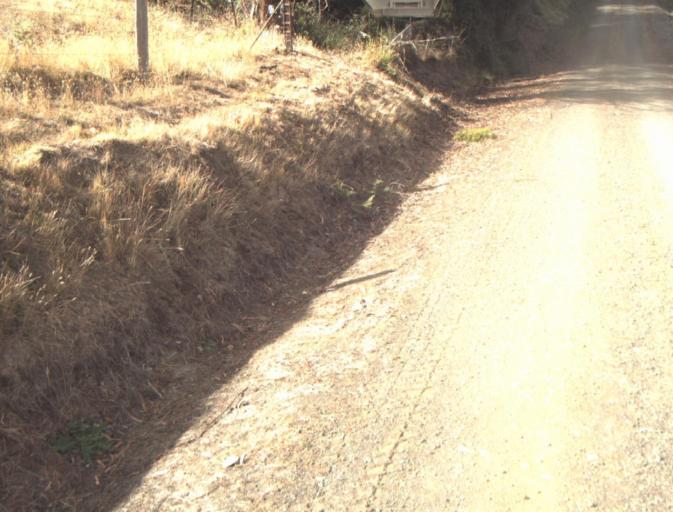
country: AU
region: Tasmania
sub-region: Launceston
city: Mayfield
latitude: -41.2954
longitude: 147.2151
